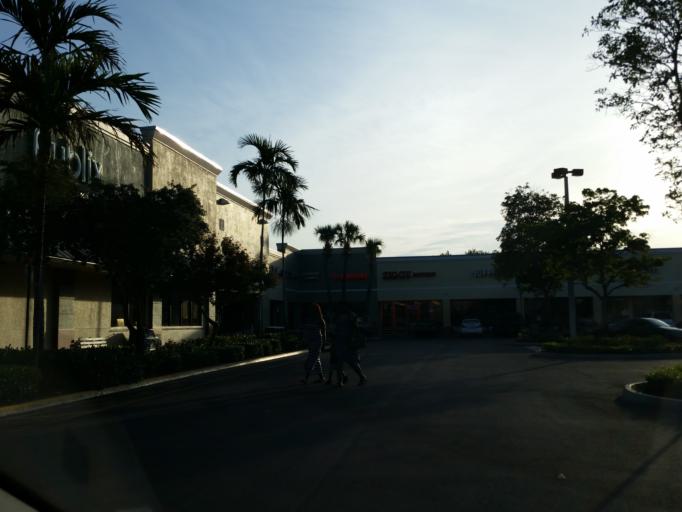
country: US
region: Florida
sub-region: Broward County
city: Cooper City
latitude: 26.0629
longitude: -80.2532
